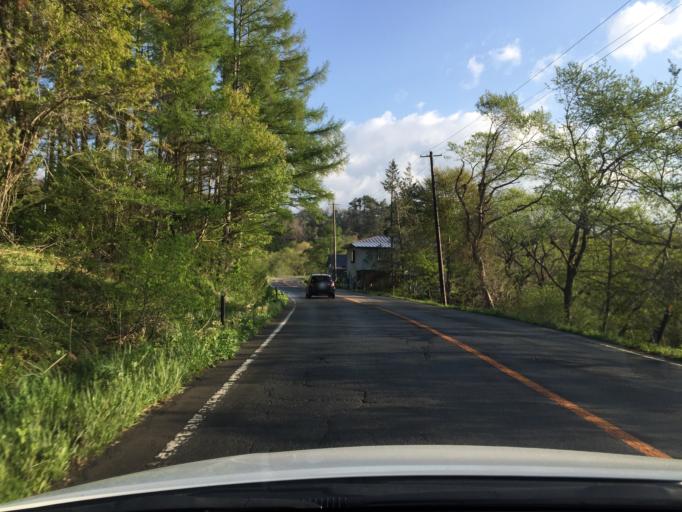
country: JP
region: Fukushima
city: Inawashiro
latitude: 37.6436
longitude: 140.0996
